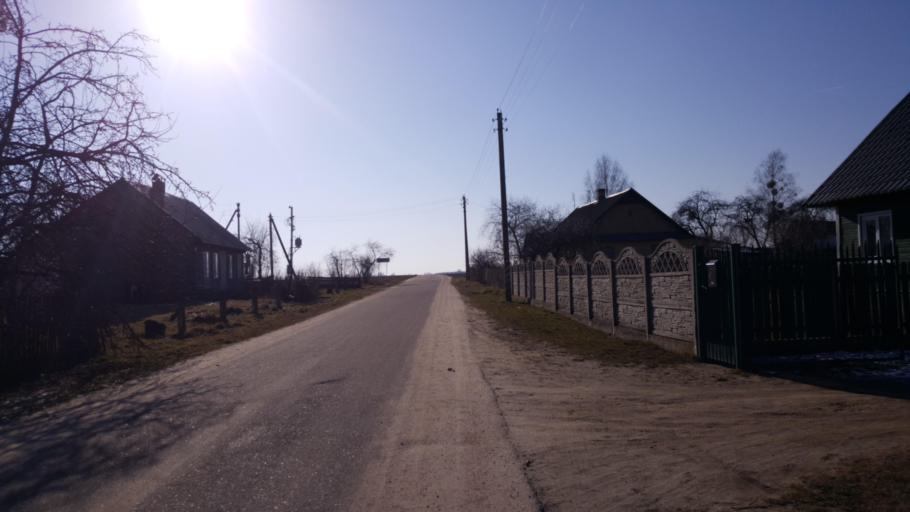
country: BY
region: Brest
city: Kamyanyets
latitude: 52.3832
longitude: 23.7949
